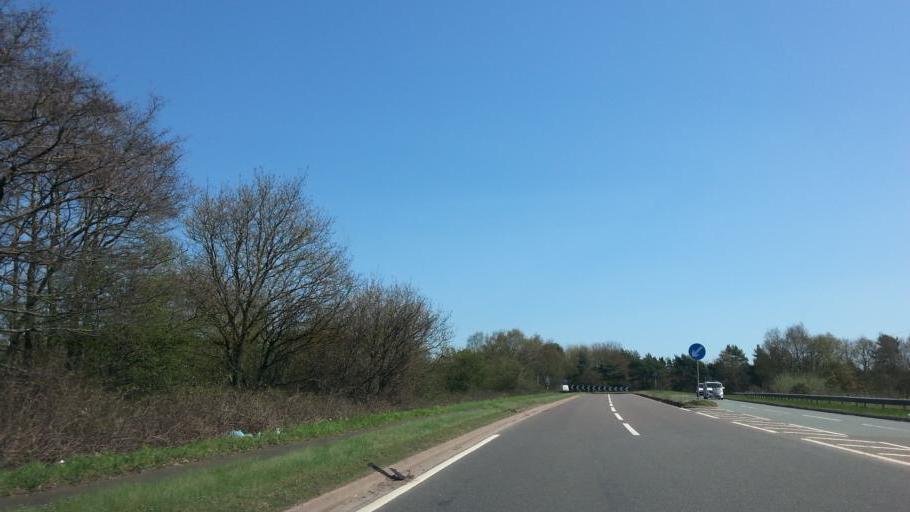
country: GB
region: England
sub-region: Staffordshire
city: Penkridge
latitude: 52.6897
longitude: -2.1073
